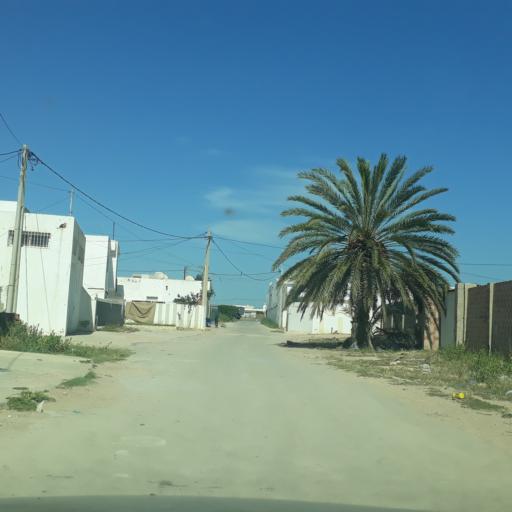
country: TN
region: Safaqis
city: Al Qarmadah
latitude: 34.8321
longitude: 10.7627
